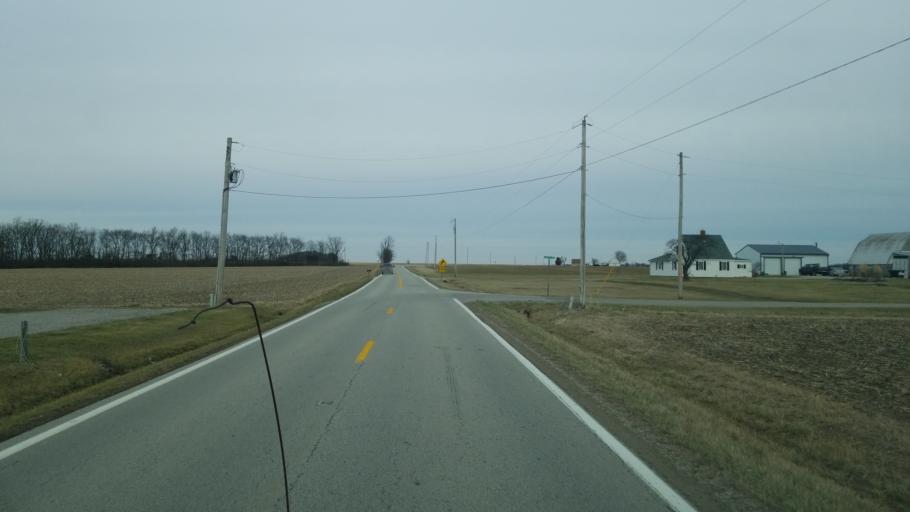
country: US
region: Ohio
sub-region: Ross County
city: Frankfort
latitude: 39.4642
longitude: -83.2052
